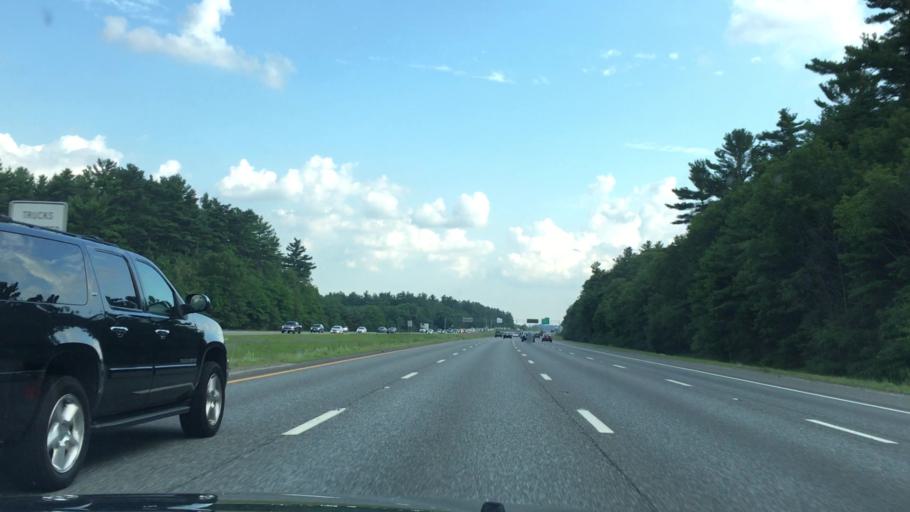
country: US
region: Massachusetts
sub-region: Essex County
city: Topsfield
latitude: 42.6400
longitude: -70.9771
